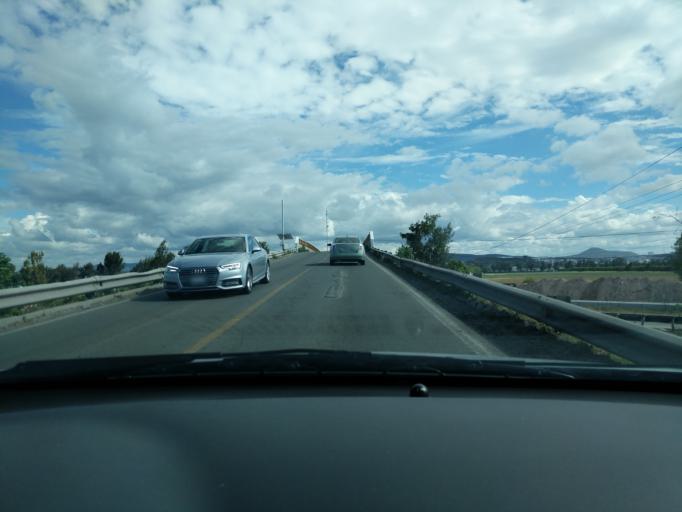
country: MX
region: Queretaro
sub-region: El Marques
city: La Loma
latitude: 20.5930
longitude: -100.2475
